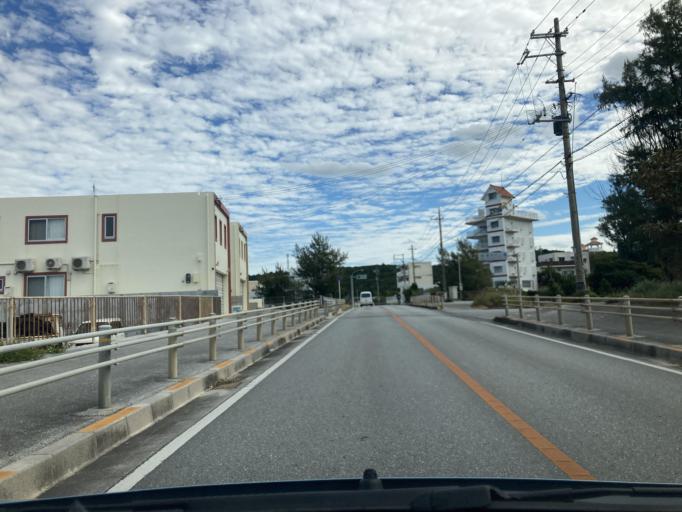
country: JP
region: Okinawa
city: Ishikawa
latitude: 26.4223
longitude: 127.7410
